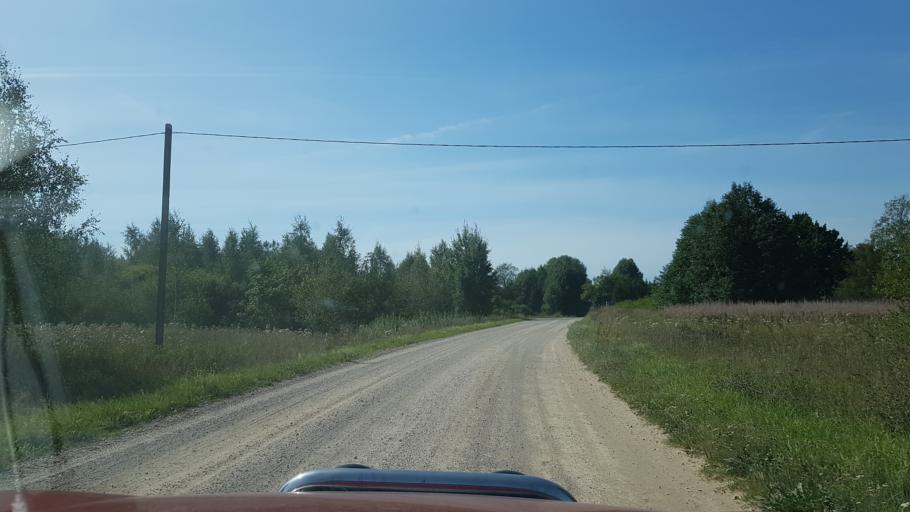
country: EE
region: Viljandimaa
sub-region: Vohma linn
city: Vohma
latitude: 58.5237
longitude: 25.6608
